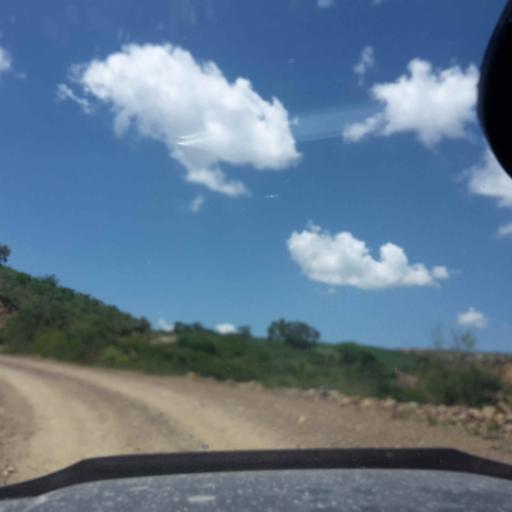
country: BO
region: Cochabamba
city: Totora
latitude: -17.7693
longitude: -65.2601
